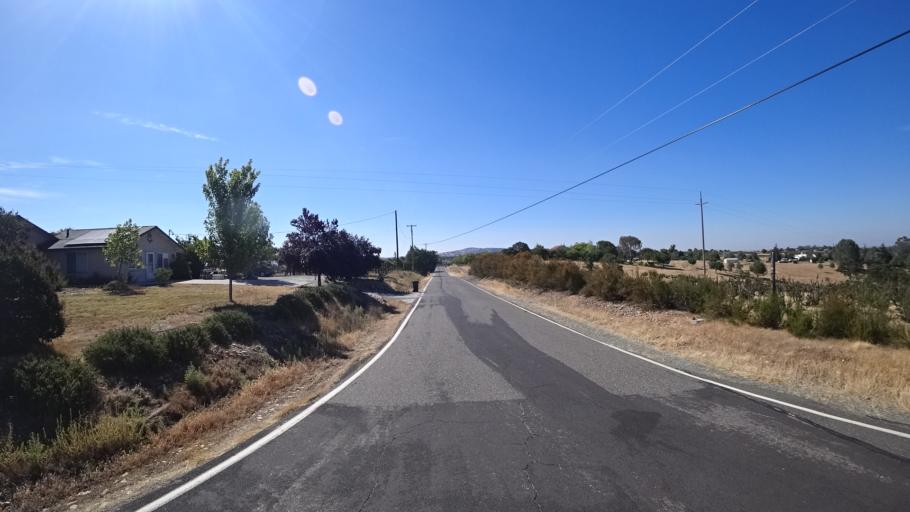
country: US
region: California
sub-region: Calaveras County
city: Rancho Calaveras
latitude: 38.1655
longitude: -120.8629
